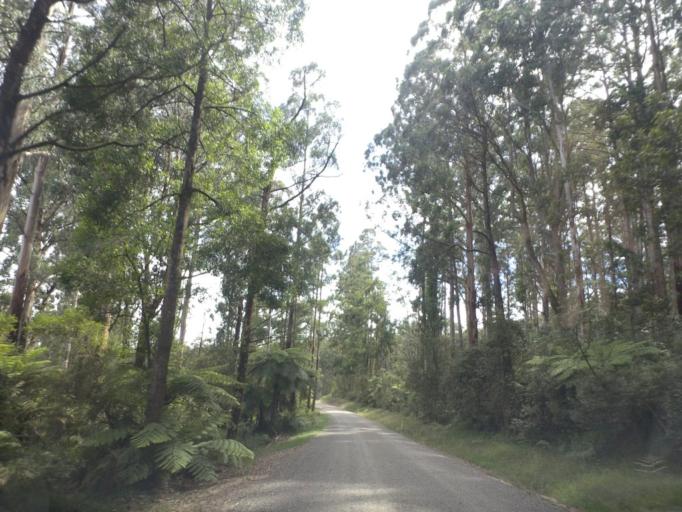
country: AU
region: Victoria
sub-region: Yarra Ranges
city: Healesville
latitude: -37.5528
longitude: 145.5135
